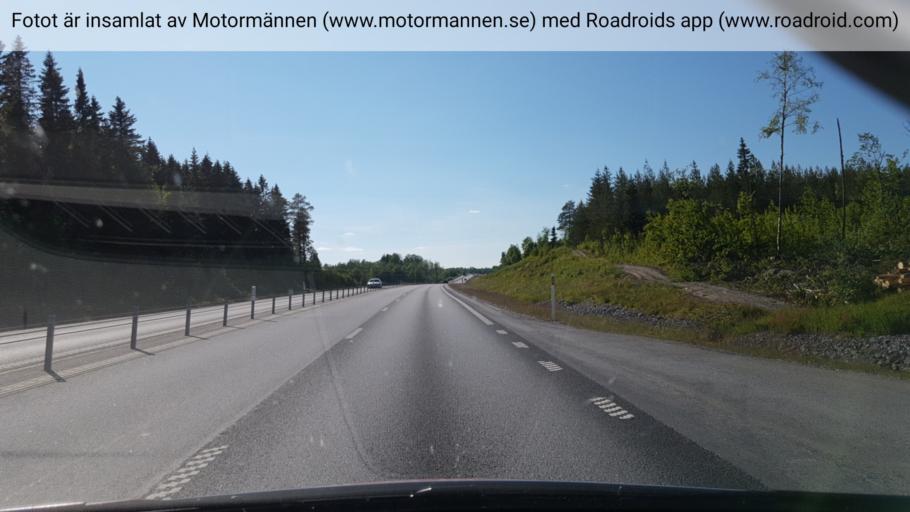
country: SE
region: Vaesterbotten
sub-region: Vannas Kommun
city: Vannasby
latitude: 63.8956
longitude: 19.9235
